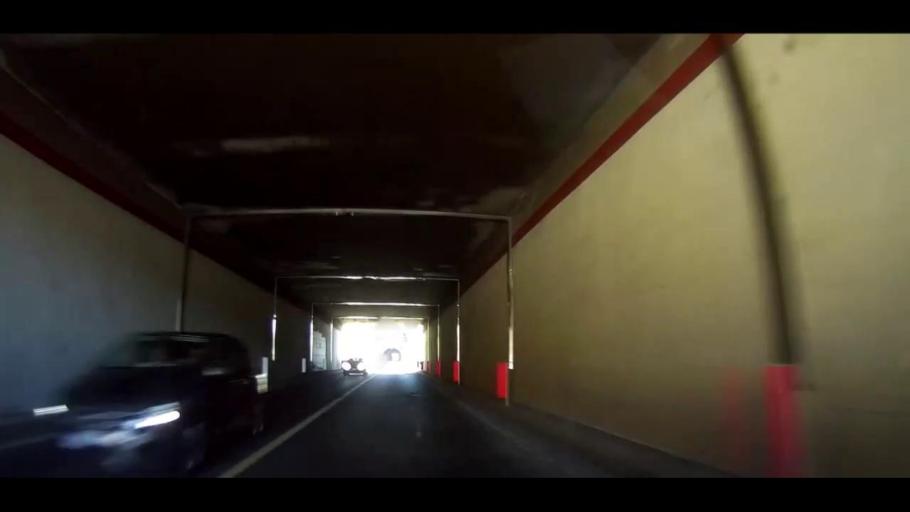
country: IT
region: Calabria
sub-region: Provincia di Cosenza
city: Celico
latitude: 39.3148
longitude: 16.3380
